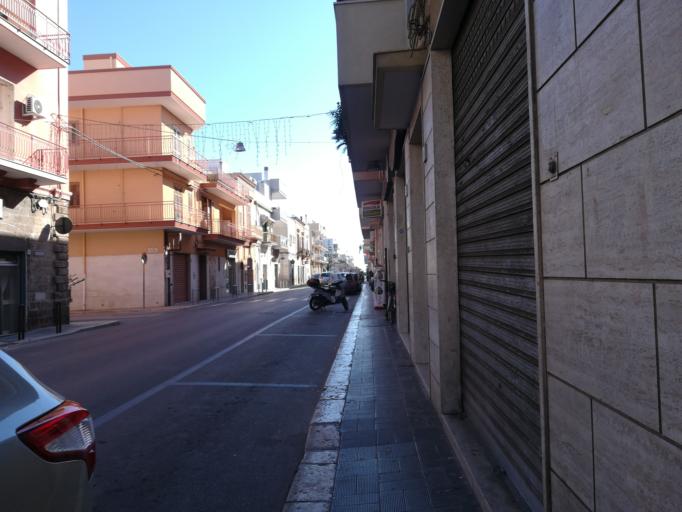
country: IT
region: Apulia
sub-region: Provincia di Bari
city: Polignano a Mare
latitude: 40.9923
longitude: 17.2245
